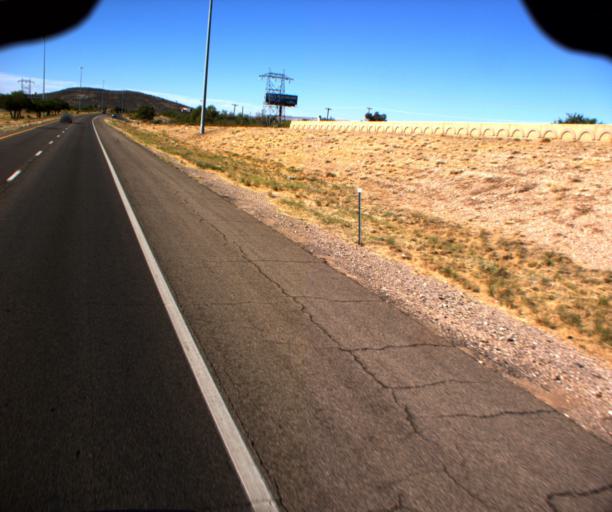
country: US
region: Arizona
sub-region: Pima County
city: Drexel Heights
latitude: 32.1329
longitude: -110.9867
